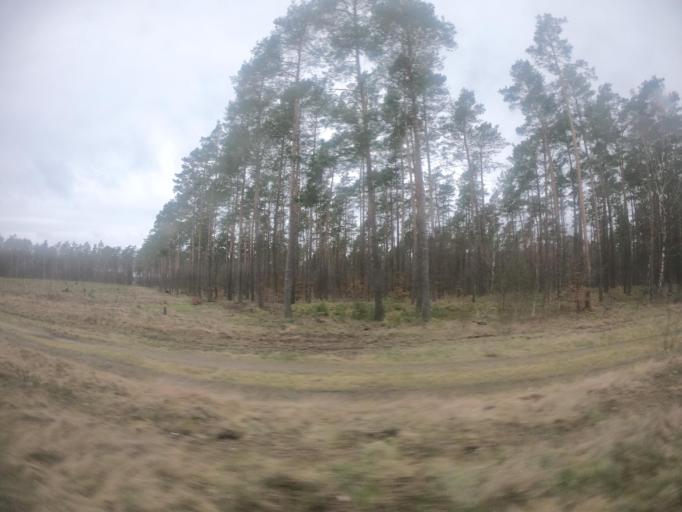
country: PL
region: West Pomeranian Voivodeship
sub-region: Powiat szczecinecki
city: Bialy Bor
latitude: 53.8202
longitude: 16.8700
